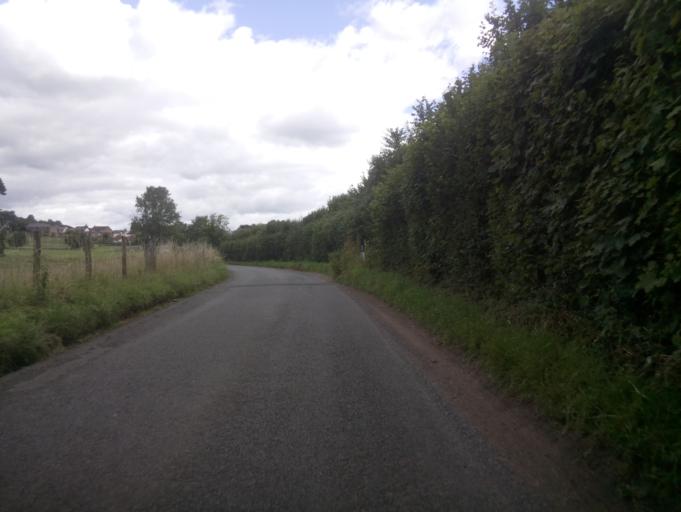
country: GB
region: England
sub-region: Gloucestershire
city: Cinderford
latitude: 51.8156
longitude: -2.4818
